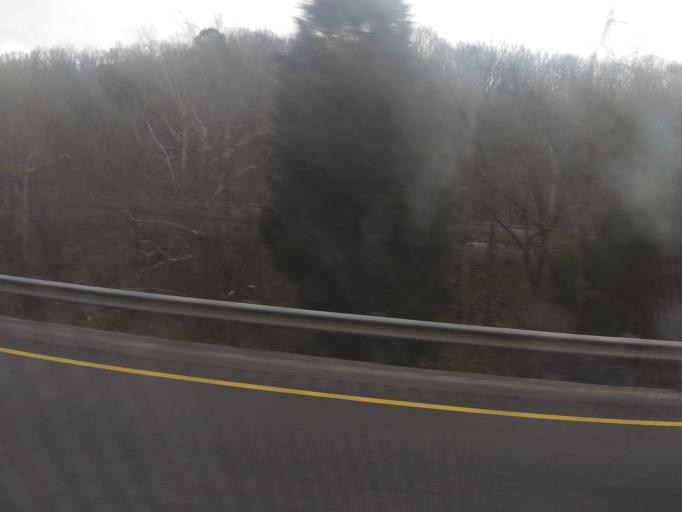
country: US
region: Tennessee
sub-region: Marion County
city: Jasper
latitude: 35.0079
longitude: -85.5279
